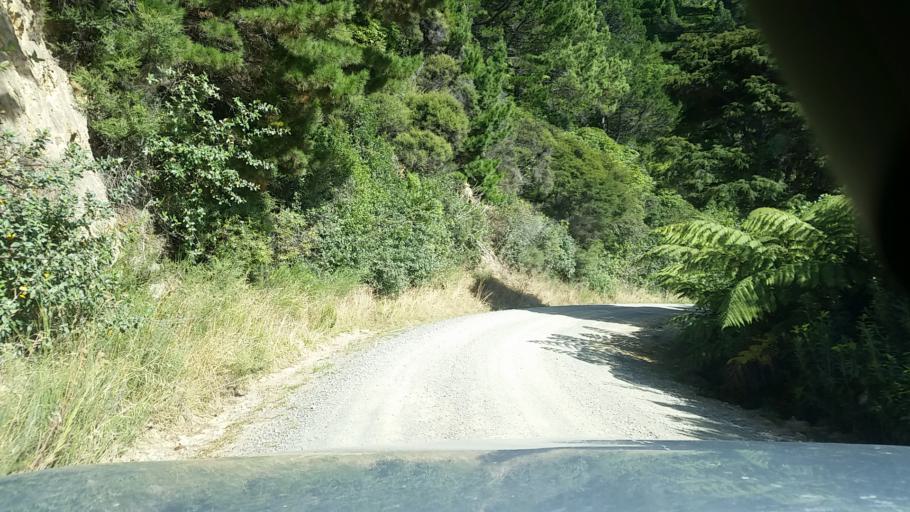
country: NZ
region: Marlborough
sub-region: Marlborough District
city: Picton
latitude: -41.2908
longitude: 174.1291
